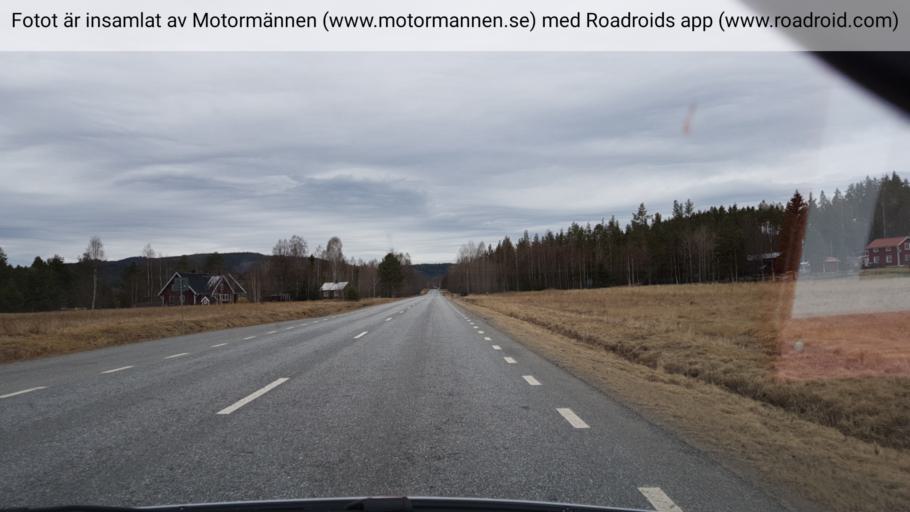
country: SE
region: Vaesternorrland
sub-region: Solleftea Kommun
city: Solleftea
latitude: 63.2628
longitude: 17.2151
